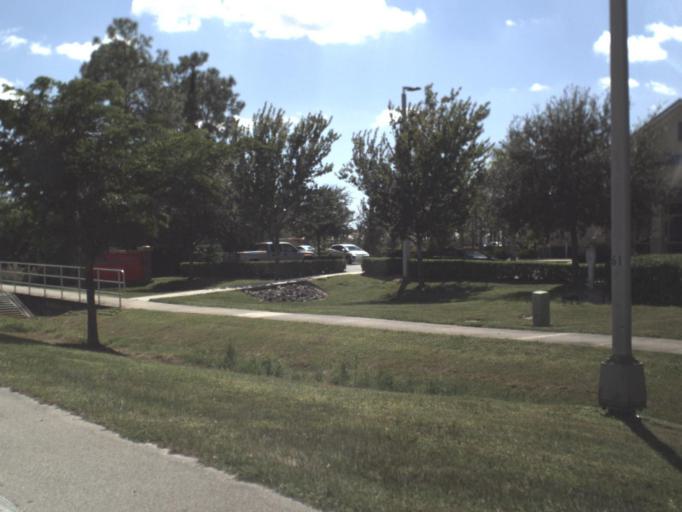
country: US
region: Florida
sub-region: Collier County
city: Lely
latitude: 26.1078
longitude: -81.7487
